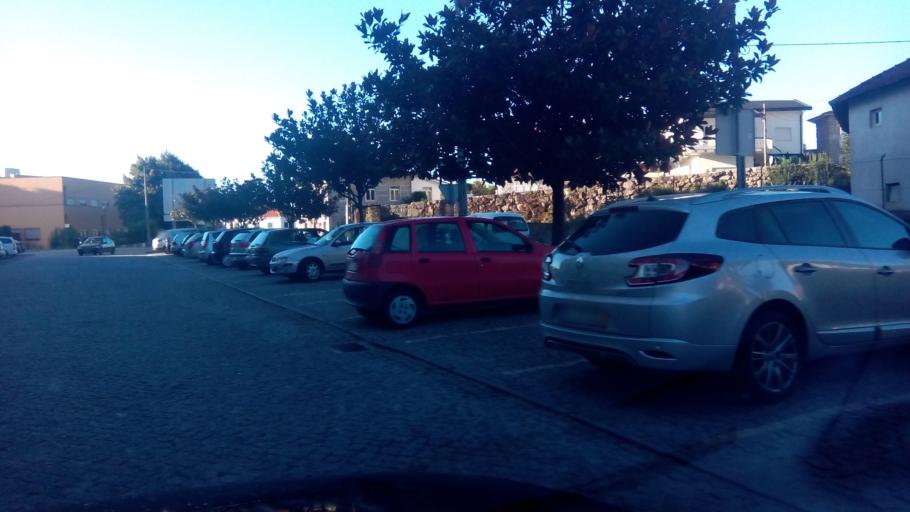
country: PT
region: Porto
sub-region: Paredes
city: Baltar
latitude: 41.1923
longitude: -8.3881
